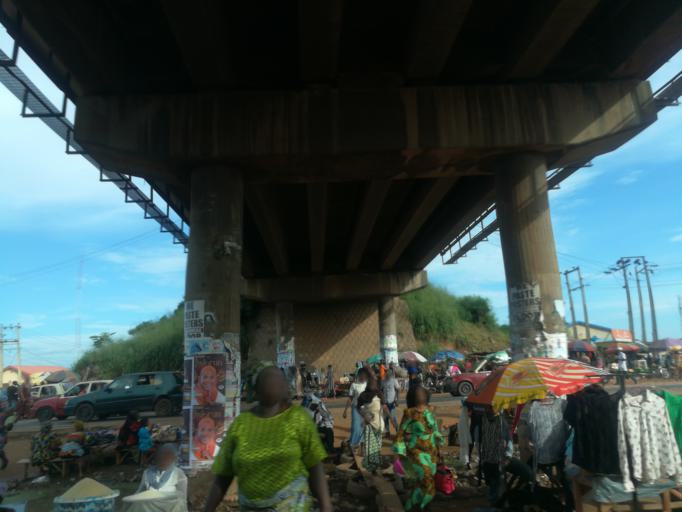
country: NG
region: Oyo
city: Ibadan
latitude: 7.3651
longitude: 3.9259
